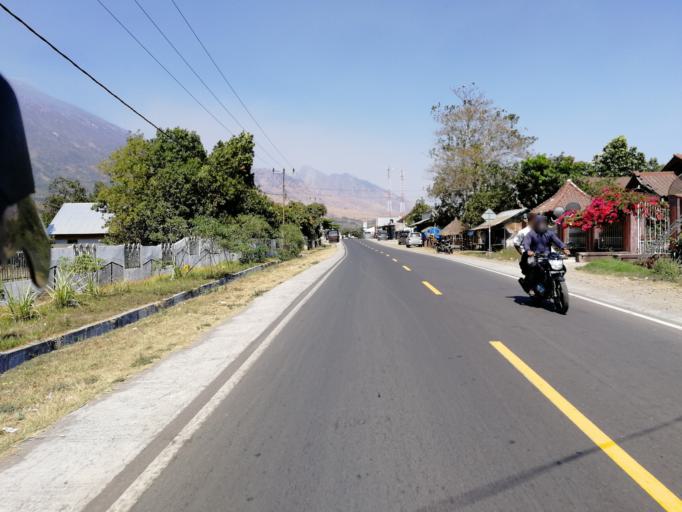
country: ID
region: West Nusa Tenggara
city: Sembalunlawang
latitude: -8.3598
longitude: 116.5285
